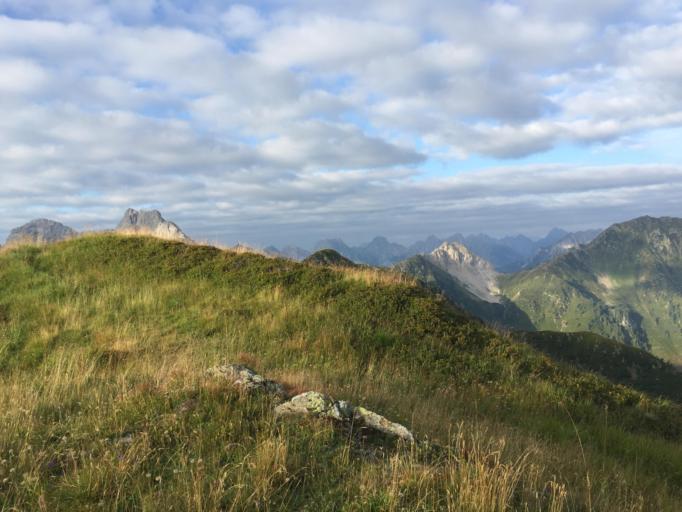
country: IT
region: Friuli Venezia Giulia
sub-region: Provincia di Udine
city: Forni Avoltri
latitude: 46.6471
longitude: 12.8446
